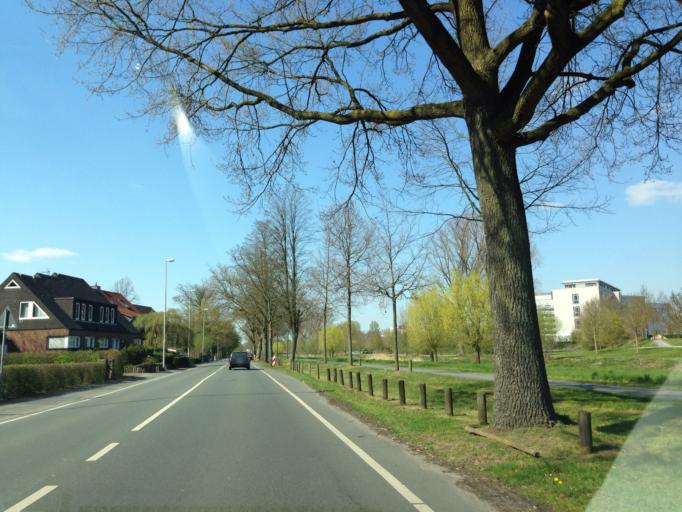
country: DE
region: North Rhine-Westphalia
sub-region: Regierungsbezirk Munster
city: Muenster
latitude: 51.9774
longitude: 7.6345
